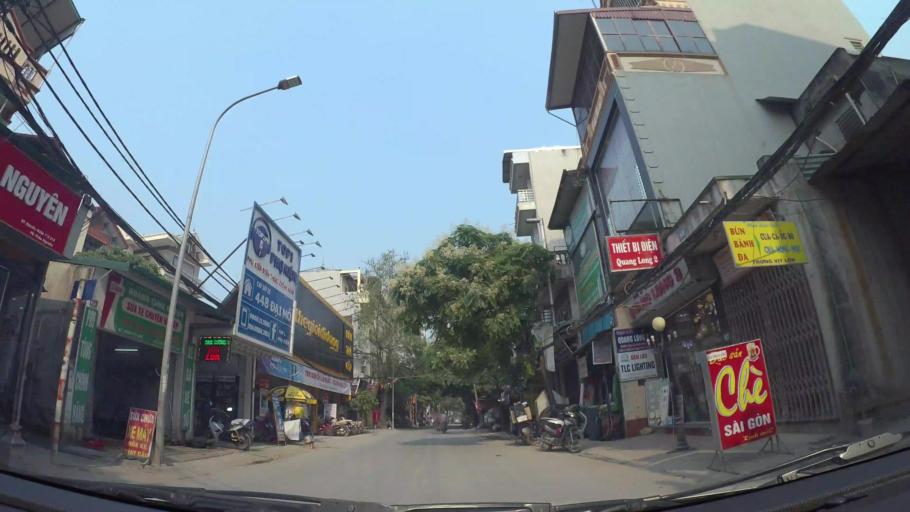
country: VN
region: Ha Noi
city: Ha Dong
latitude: 20.9956
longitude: 105.7549
